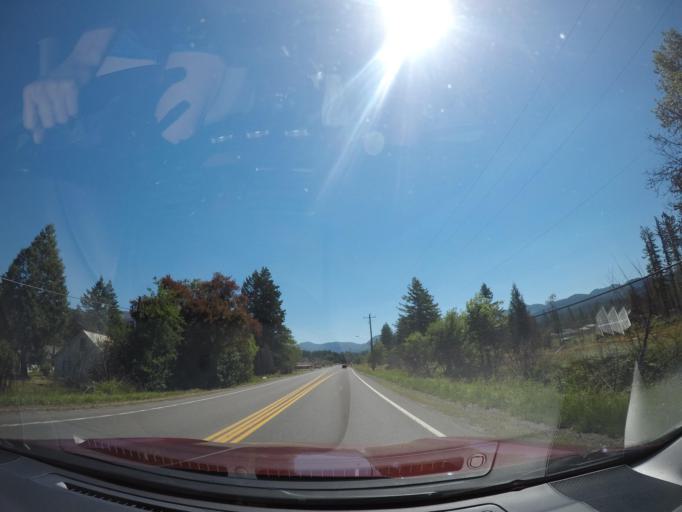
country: US
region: Oregon
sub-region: Linn County
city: Mill City
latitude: 44.7563
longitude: -122.4225
